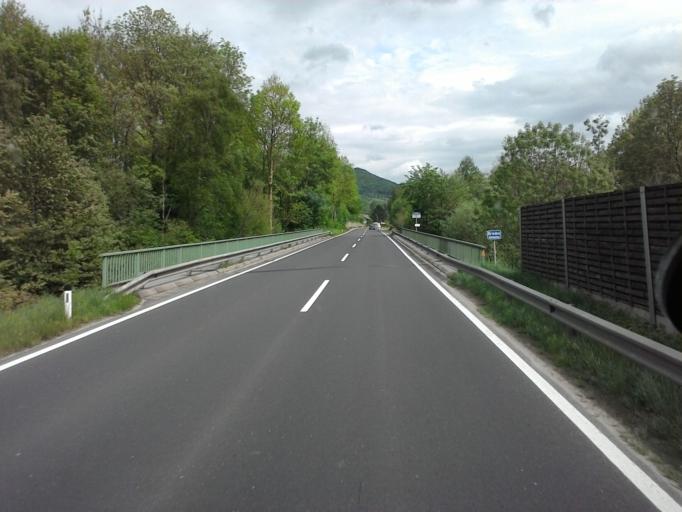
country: AT
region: Upper Austria
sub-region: Politischer Bezirk Kirchdorf an der Krems
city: Micheldorf in Oberoesterreich
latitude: 47.9239
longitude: 14.0930
